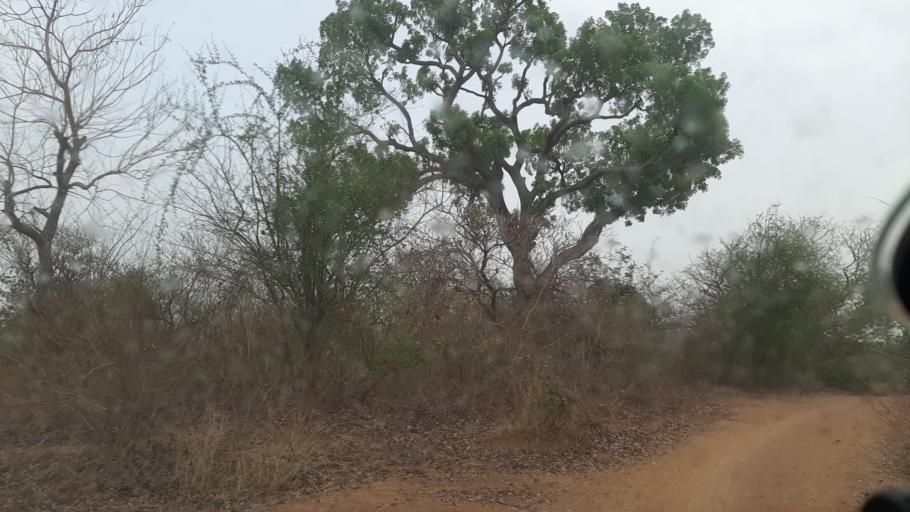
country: BF
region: Boucle du Mouhoun
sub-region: Province des Banwa
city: Salanso
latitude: 11.8620
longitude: -4.4367
